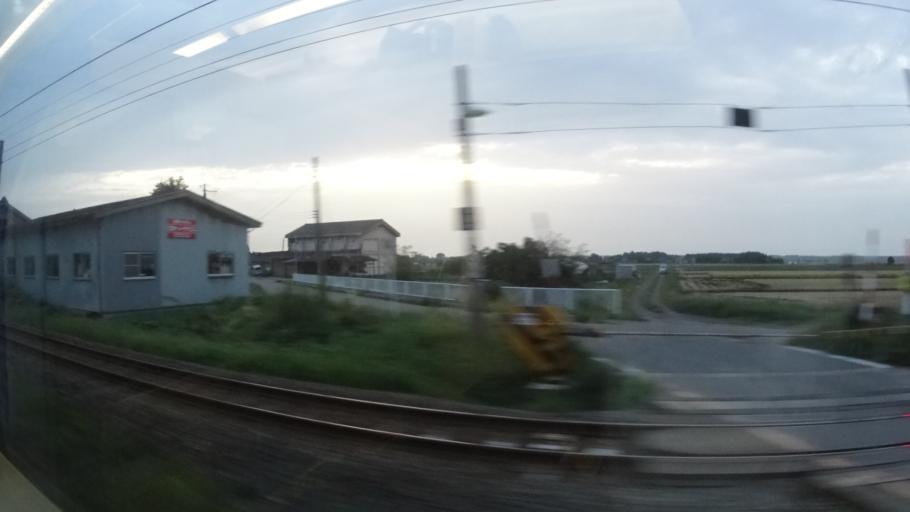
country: JP
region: Niigata
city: Murakami
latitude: 38.0922
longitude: 139.4264
